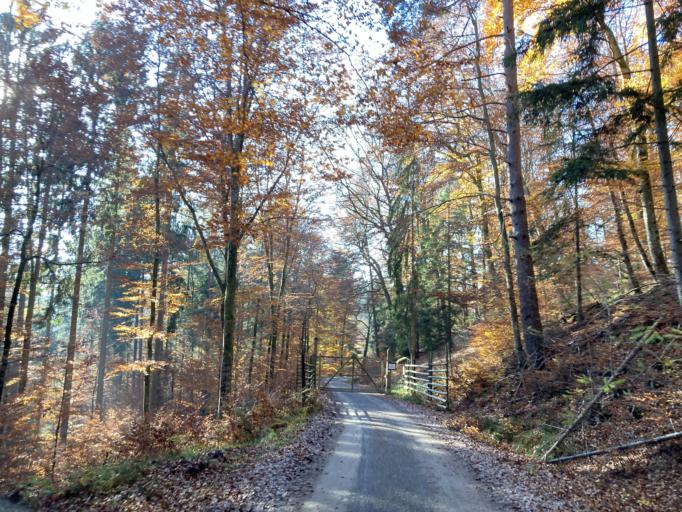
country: DE
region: Baden-Wuerttemberg
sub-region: Regierungsbezirk Stuttgart
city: Hildrizhausen
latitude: 48.5704
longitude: 8.9935
